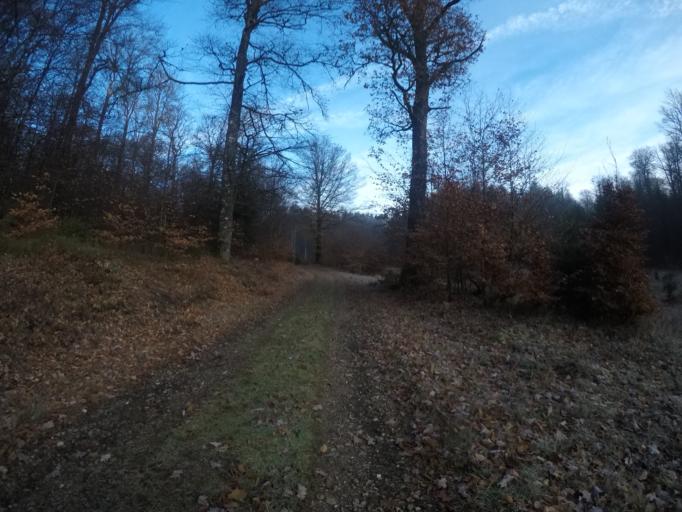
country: BE
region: Wallonia
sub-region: Province du Luxembourg
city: Habay-la-Vieille
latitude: 49.7622
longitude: 5.6600
